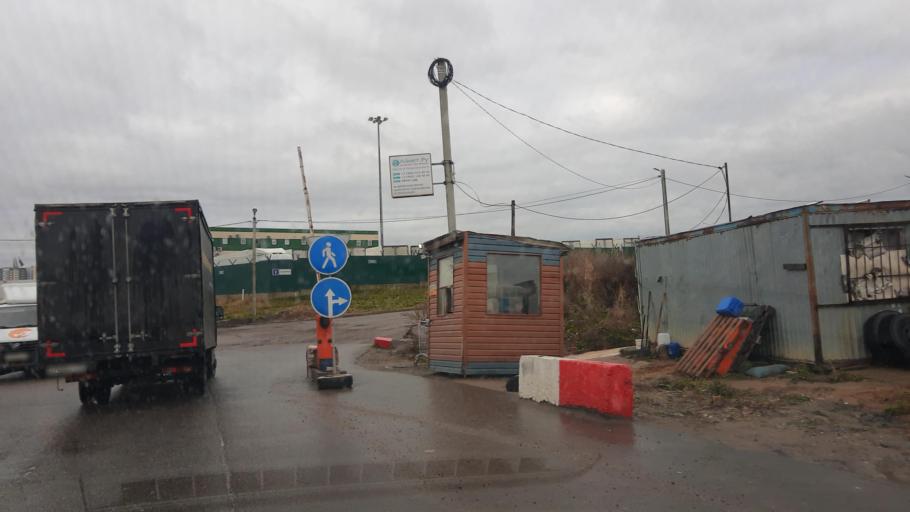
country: RU
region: Moskovskaya
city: Mosrentgen
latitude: 55.6004
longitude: 37.4575
